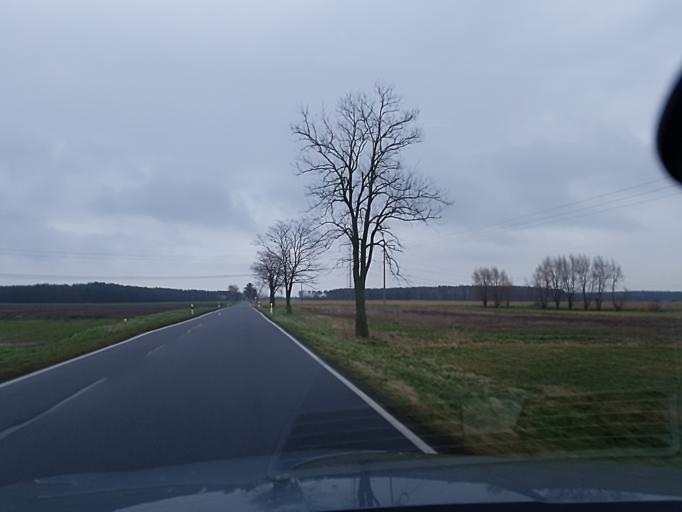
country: DE
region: Brandenburg
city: Schilda
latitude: 51.6155
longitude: 13.3653
